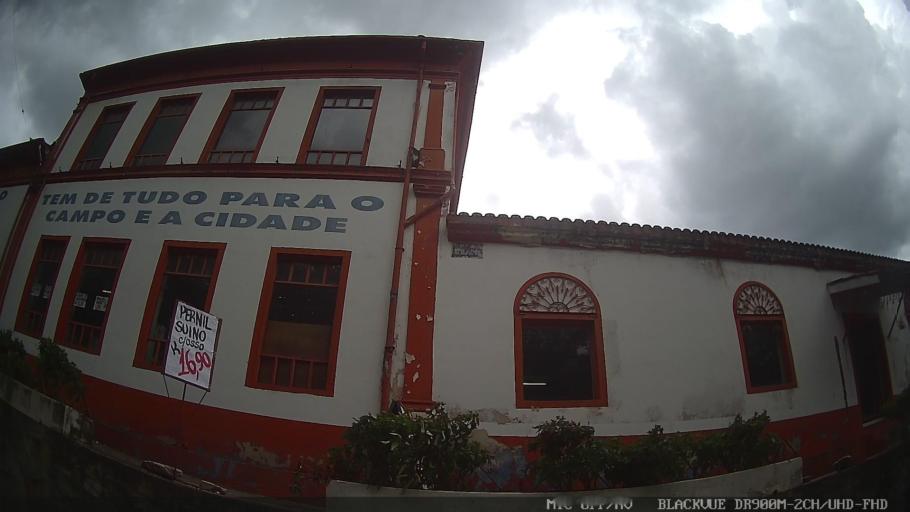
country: BR
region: Sao Paulo
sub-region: Serra Negra
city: Serra Negra
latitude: -22.6076
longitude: -46.7046
